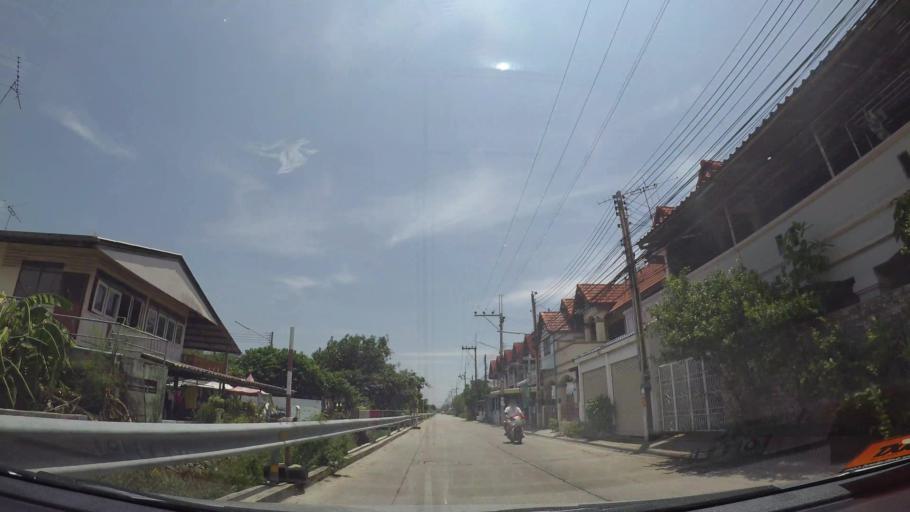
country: TH
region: Chon Buri
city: Chon Buri
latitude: 13.3255
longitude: 100.9434
